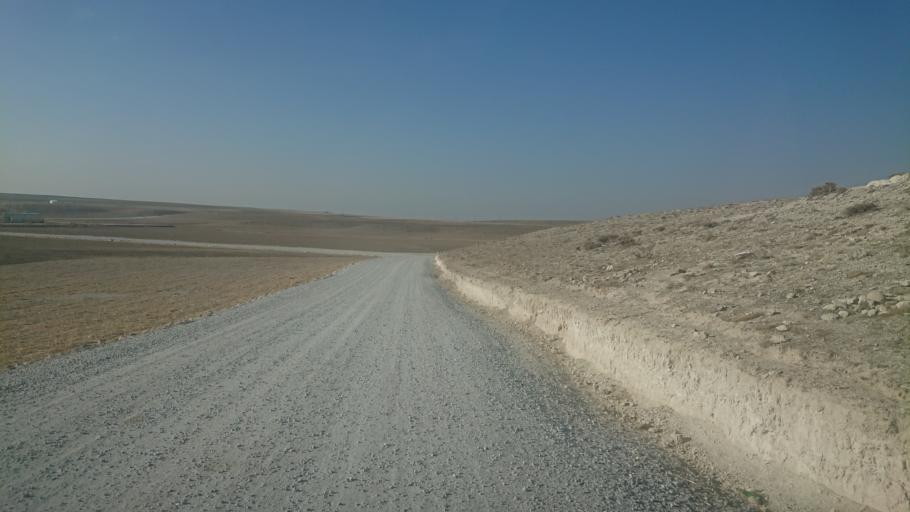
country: TR
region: Aksaray
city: Sultanhani
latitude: 38.0826
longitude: 33.6219
